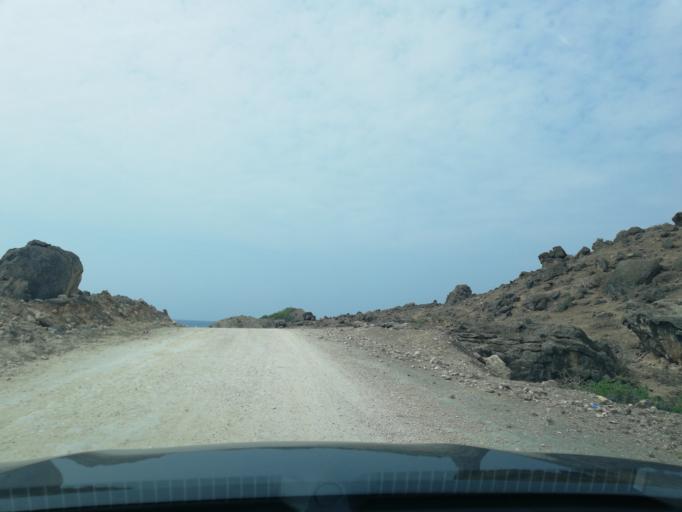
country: OM
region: Zufar
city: Salalah
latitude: 16.8358
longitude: 53.7160
